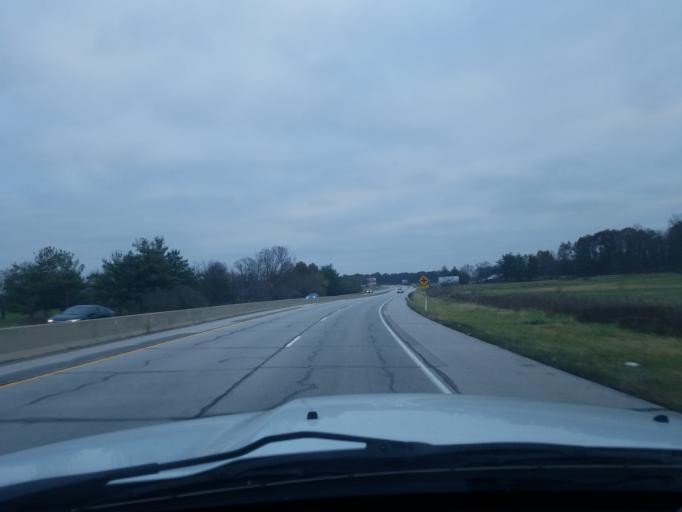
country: US
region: Indiana
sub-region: Delaware County
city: Yorktown
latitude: 40.2218
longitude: -85.5234
